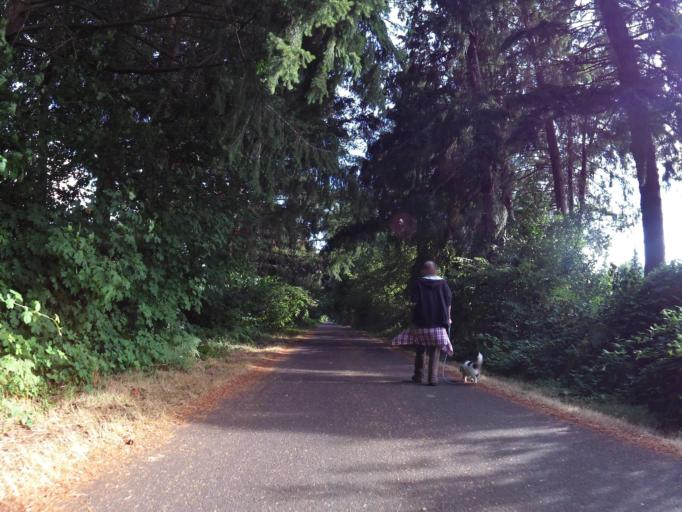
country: US
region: Washington
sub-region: Thurston County
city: Lacey
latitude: 47.0270
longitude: -122.8363
